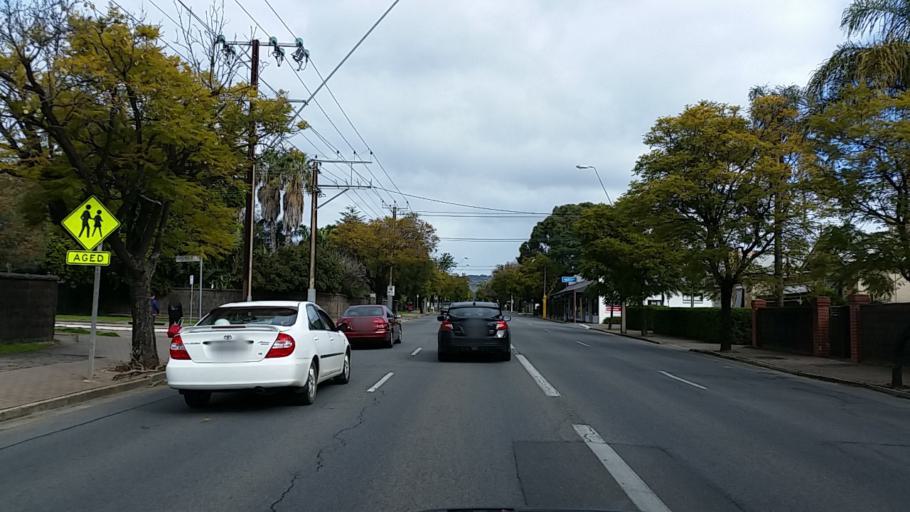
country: AU
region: South Australia
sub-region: Unley
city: Fullarton
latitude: -34.9505
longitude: 138.6254
